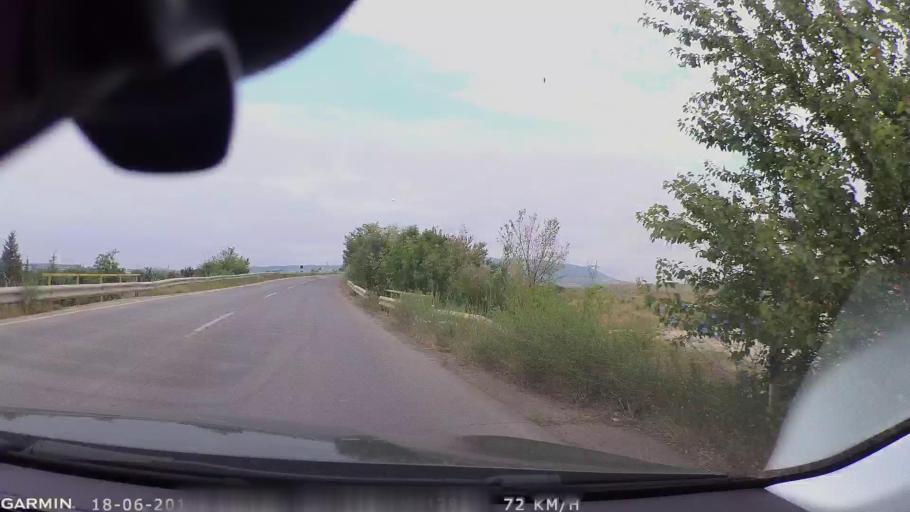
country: MK
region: Stip
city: Shtip
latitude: 41.7723
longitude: 22.1782
